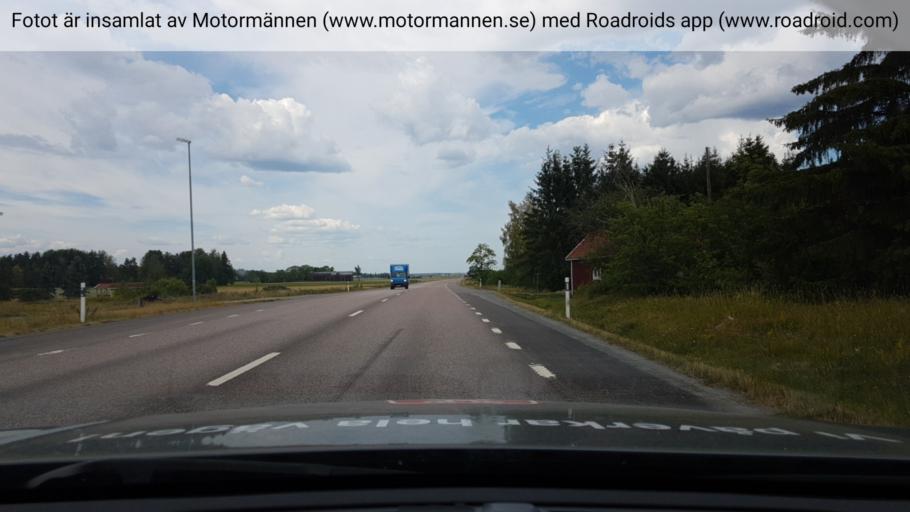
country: SE
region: Vaestmanland
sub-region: Sala Kommun
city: Sala
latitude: 59.8727
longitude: 16.6271
